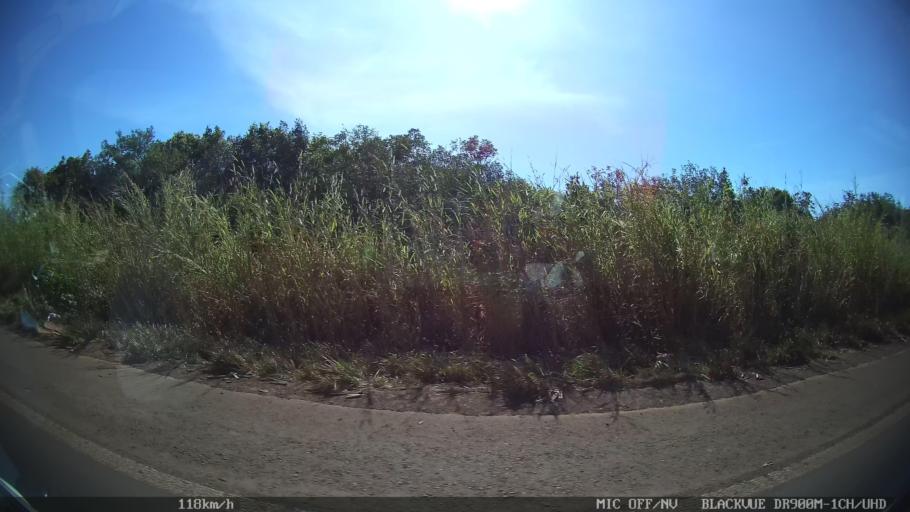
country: BR
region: Sao Paulo
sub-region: Barretos
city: Barretos
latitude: -20.5604
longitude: -48.6518
